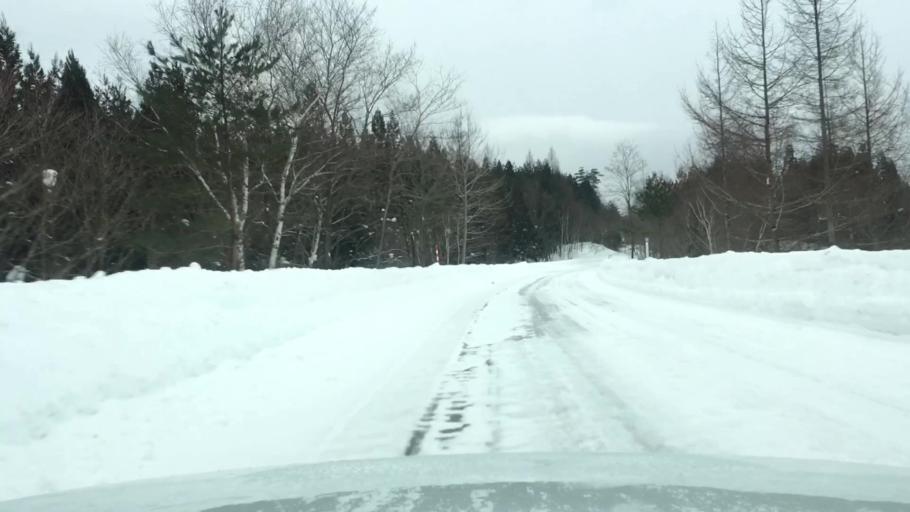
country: JP
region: Akita
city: Hanawa
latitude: 39.9887
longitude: 140.9976
